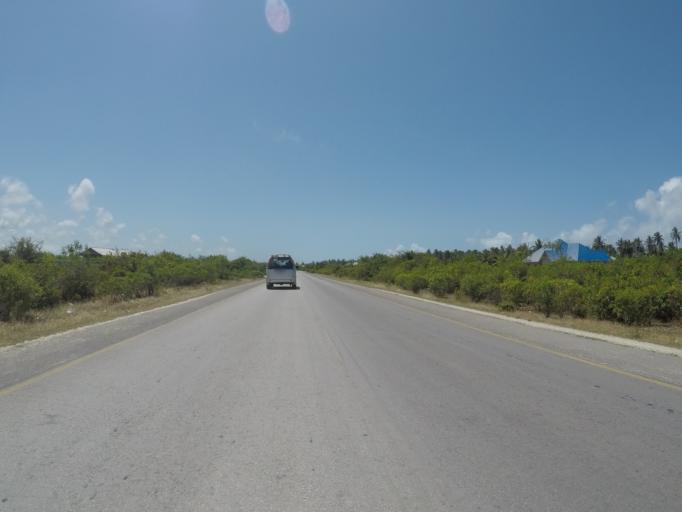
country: TZ
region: Zanzibar Central/South
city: Nganane
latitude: -6.3158
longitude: 39.5421
